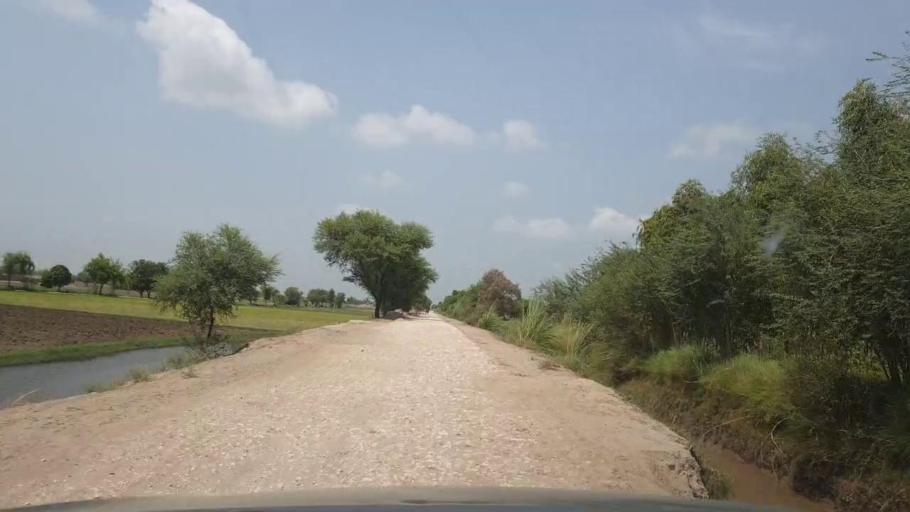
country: PK
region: Sindh
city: Ratodero
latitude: 27.8925
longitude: 68.3045
